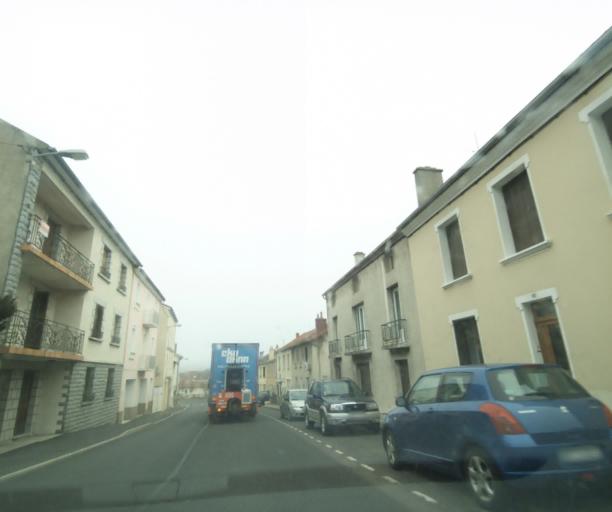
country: FR
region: Languedoc-Roussillon
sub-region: Departement de la Lozere
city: Langogne
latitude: 44.7223
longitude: 3.8492
